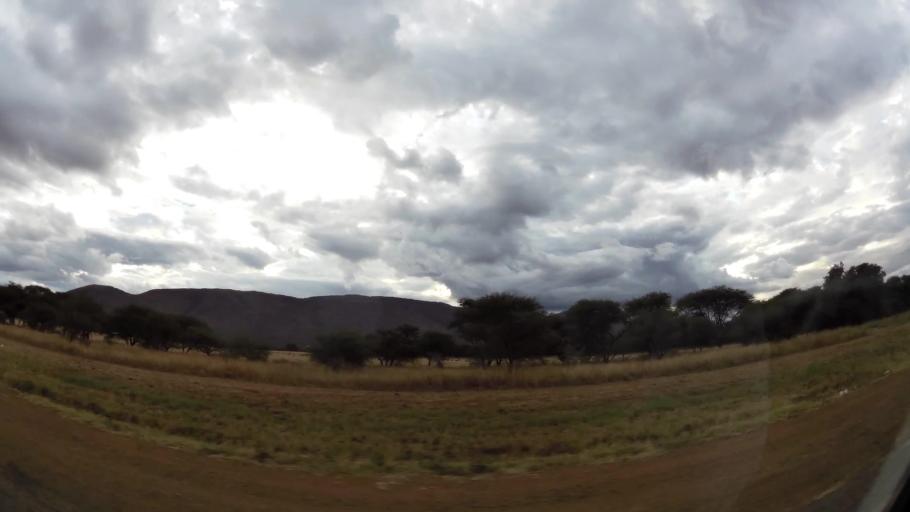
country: ZA
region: Limpopo
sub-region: Waterberg District Municipality
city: Mokopane
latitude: -24.2420
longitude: 28.9942
